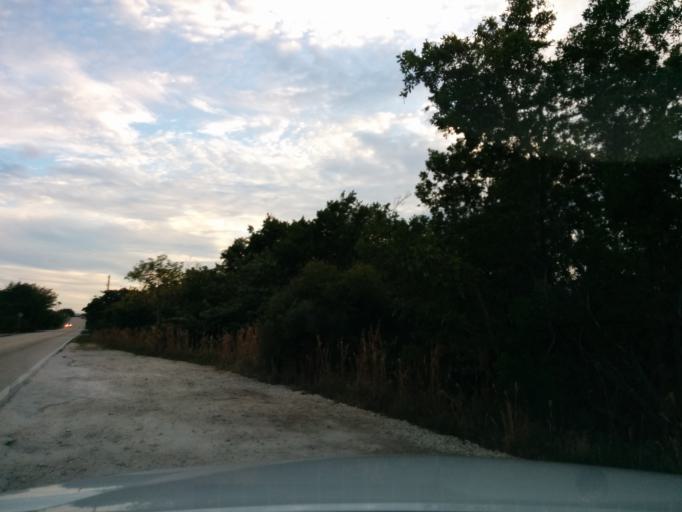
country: US
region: Florida
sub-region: Broward County
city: Dania Beach
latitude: 26.0590
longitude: -80.1138
